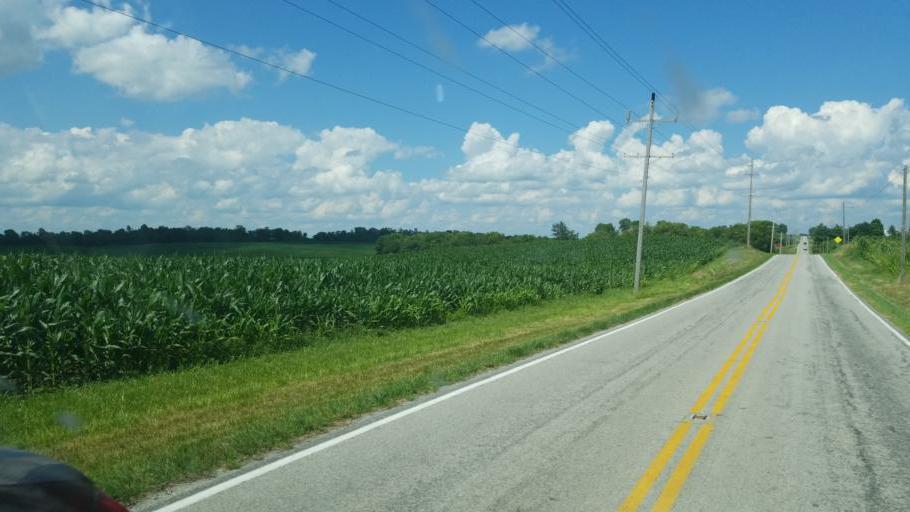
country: US
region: Ohio
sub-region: Highland County
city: Greenfield
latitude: 39.2664
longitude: -83.4399
